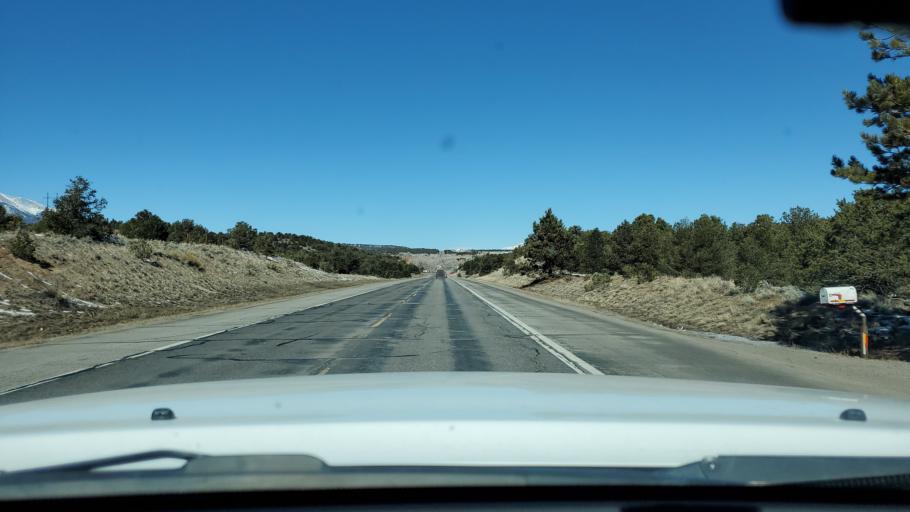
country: US
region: Colorado
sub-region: Chaffee County
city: Salida
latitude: 38.6285
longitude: -106.0781
